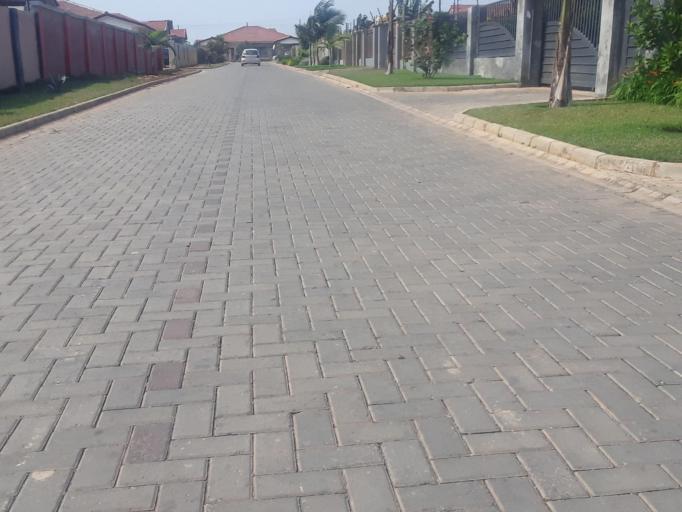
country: ZM
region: Lusaka
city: Lusaka
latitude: -15.3605
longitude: 28.2800
